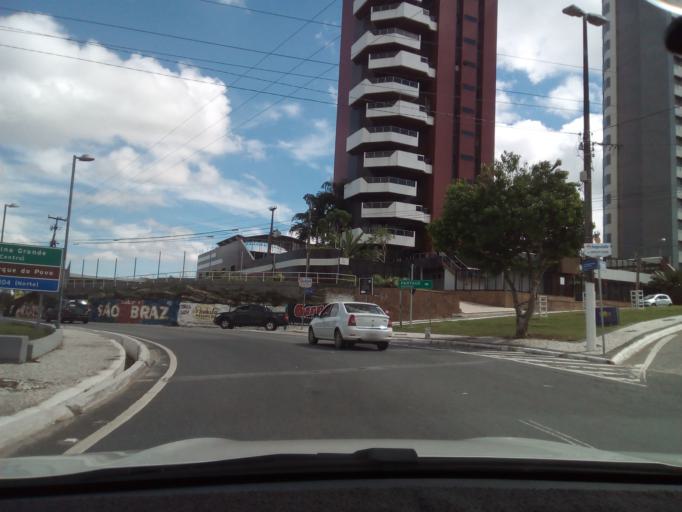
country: BR
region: Paraiba
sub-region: Campina Grande
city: Campina Grande
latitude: -7.2367
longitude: -35.8671
